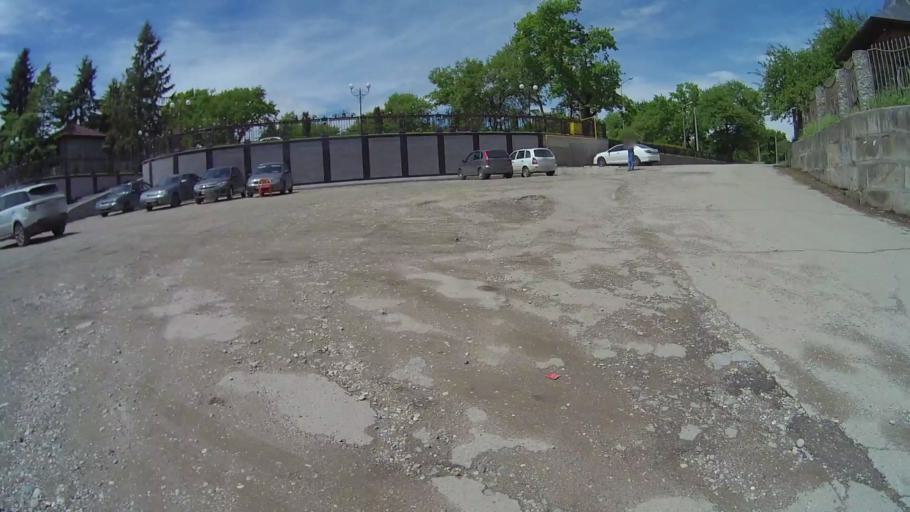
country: RU
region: Kabardino-Balkariya
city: Vol'nyy Aul
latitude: 43.4595
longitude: 43.5895
